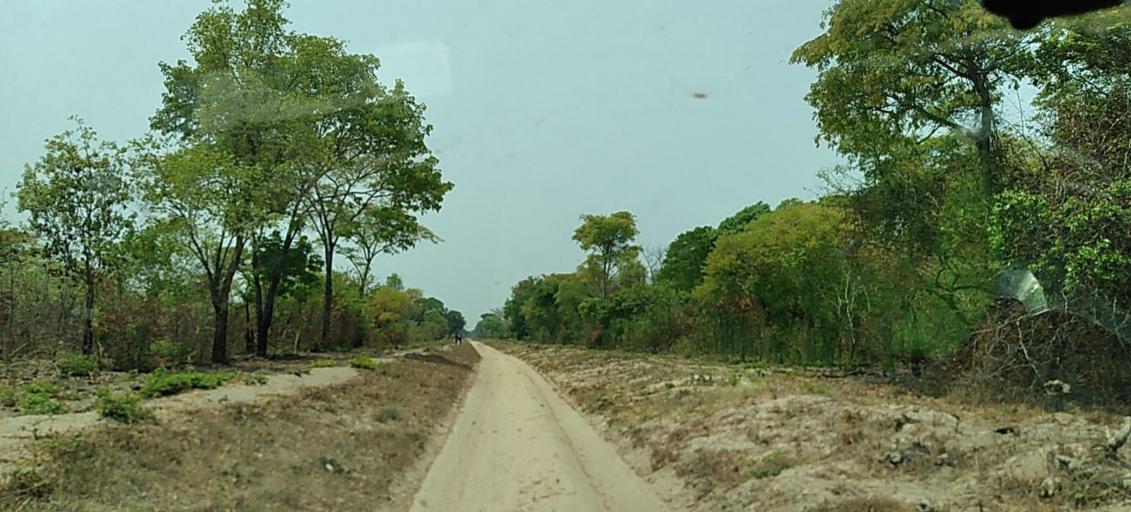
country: ZM
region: Western
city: Lukulu
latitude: -14.1479
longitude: 23.2920
